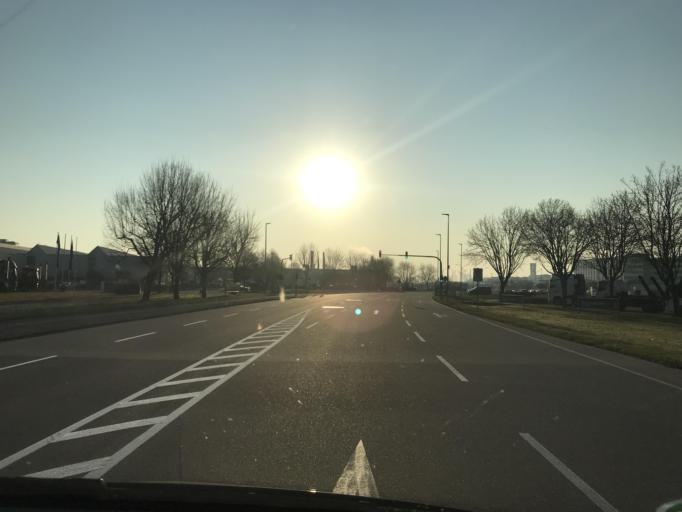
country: DE
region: Rheinland-Pfalz
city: Worth am Rhein
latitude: 49.0522
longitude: 8.2774
